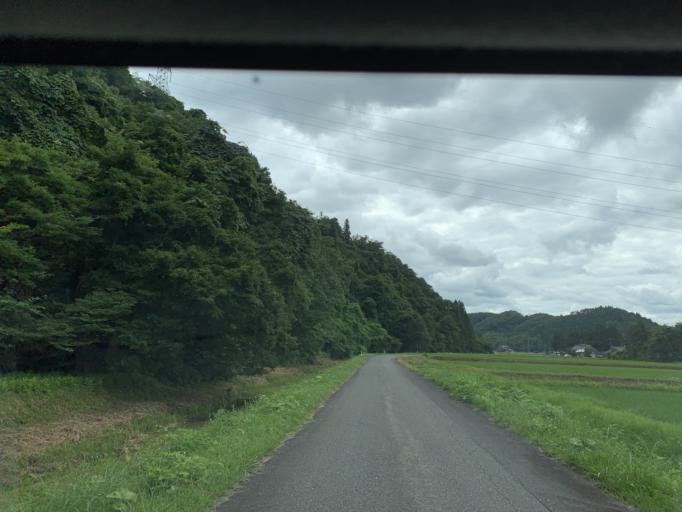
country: JP
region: Iwate
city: Ichinoseki
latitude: 38.9463
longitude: 141.0195
